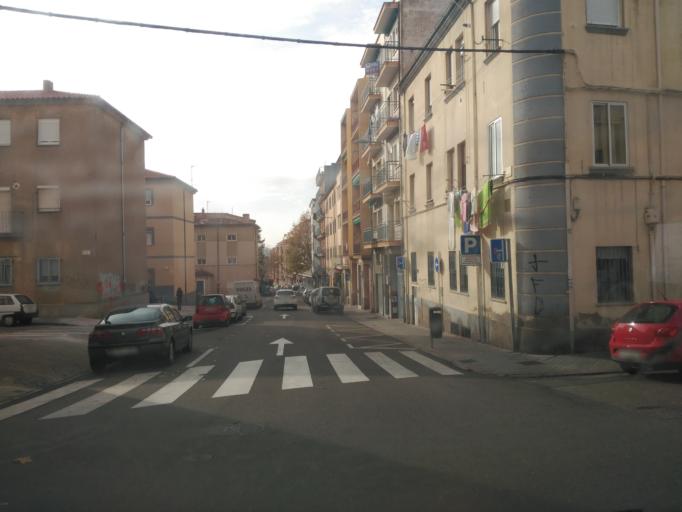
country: ES
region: Castille and Leon
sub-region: Provincia de Salamanca
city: Salamanca
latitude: 40.9696
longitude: -5.6718
